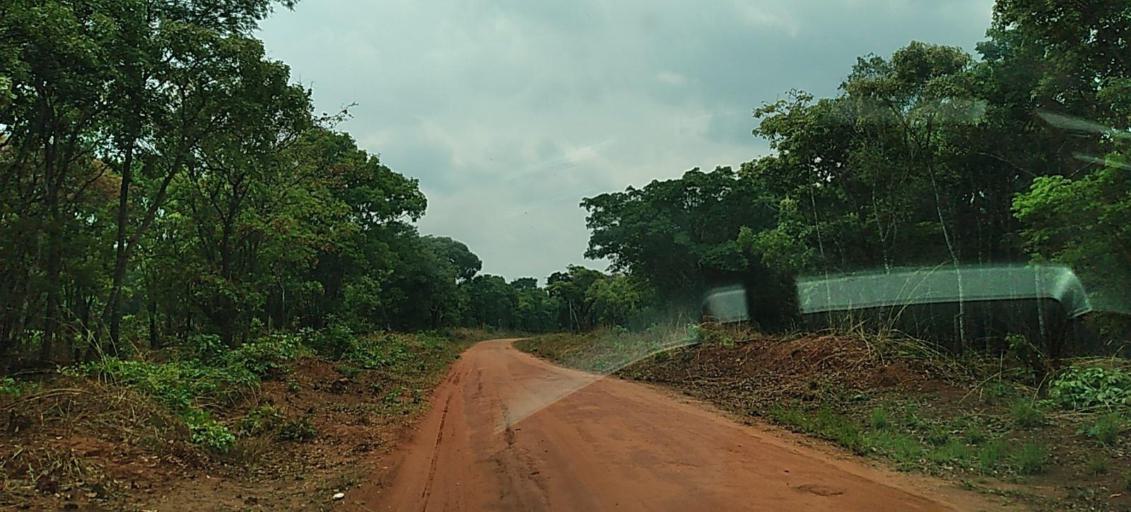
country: ZM
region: North-Western
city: Mwinilunga
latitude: -11.5536
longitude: 24.7734
